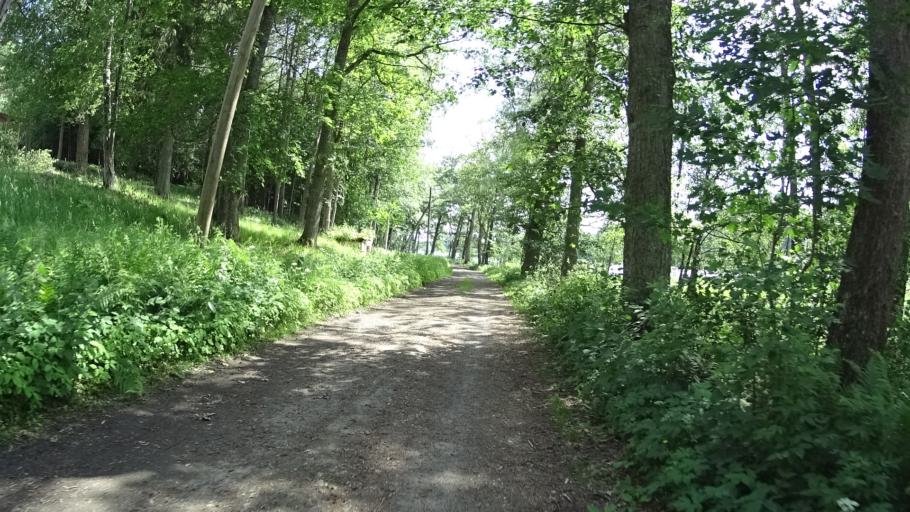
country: FI
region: Uusimaa
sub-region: Raaseporin
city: Pohja
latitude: 60.1210
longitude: 23.5390
